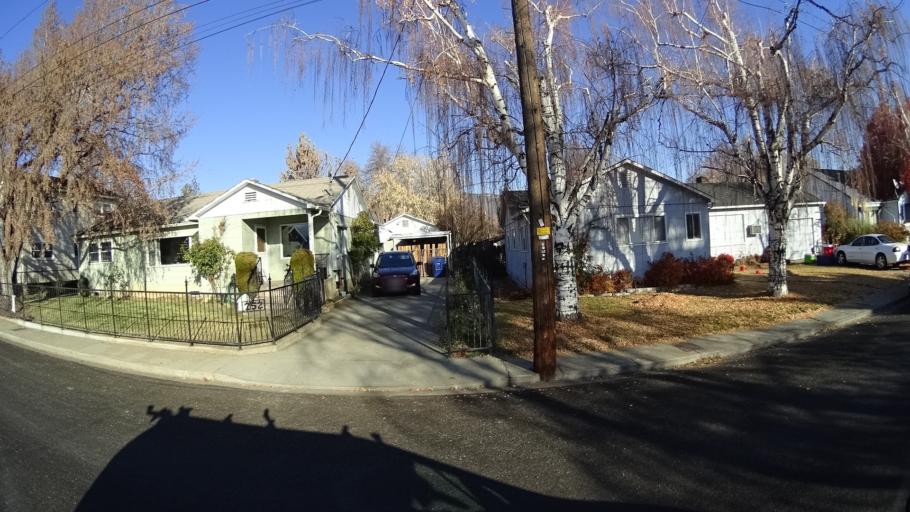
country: US
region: California
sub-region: Siskiyou County
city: Yreka
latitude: 41.7278
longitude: -122.6465
